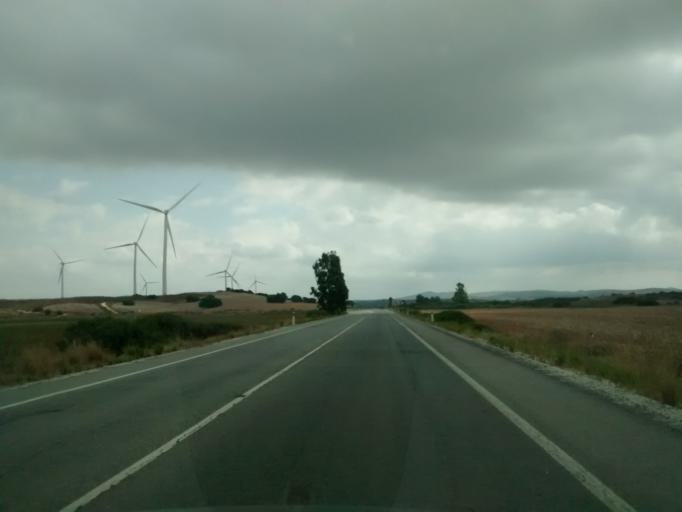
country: ES
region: Andalusia
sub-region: Provincia de Cadiz
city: Chiclana de la Frontera
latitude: 36.4172
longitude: -6.0886
